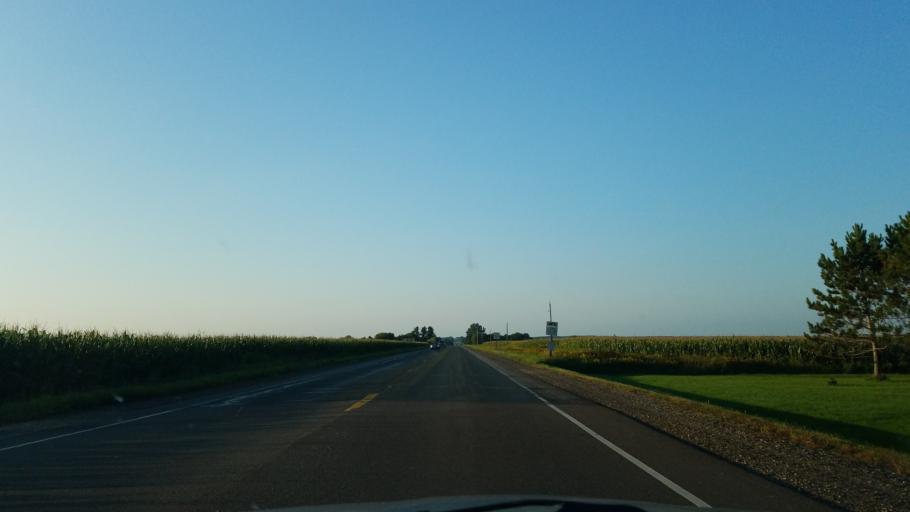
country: US
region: Wisconsin
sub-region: Polk County
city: Clear Lake
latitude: 45.2096
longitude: -92.2840
